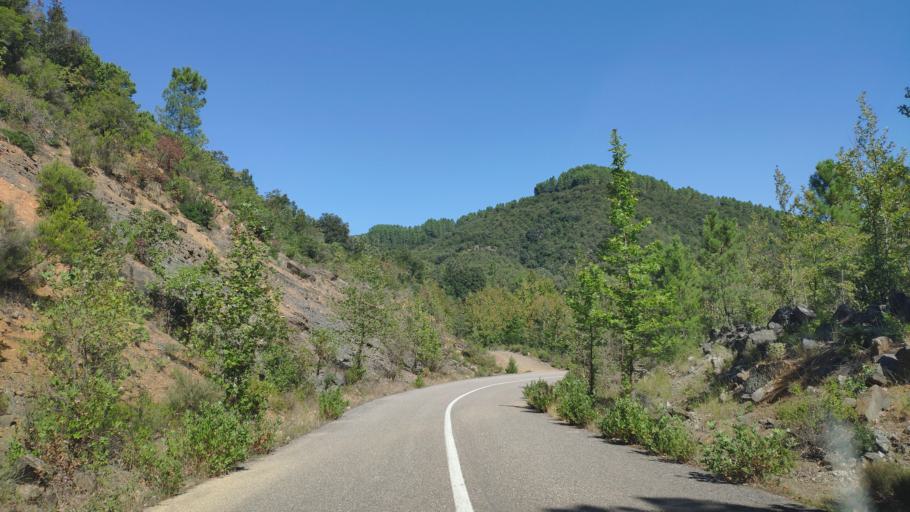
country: GR
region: Central Greece
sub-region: Nomos Evrytanias
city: Kerasochori
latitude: 38.9909
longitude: 21.5047
